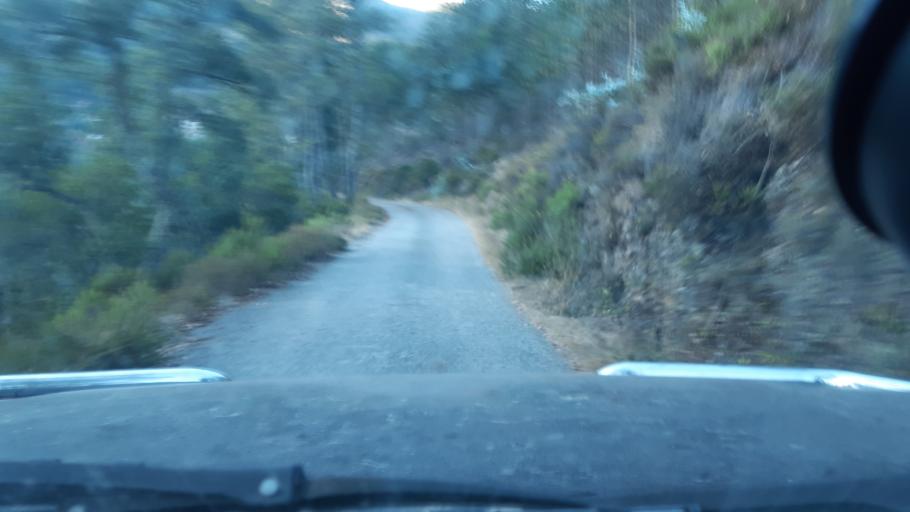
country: PT
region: Viseu
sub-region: Mortagua
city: Mortagua
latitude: 40.5289
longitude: -8.2543
